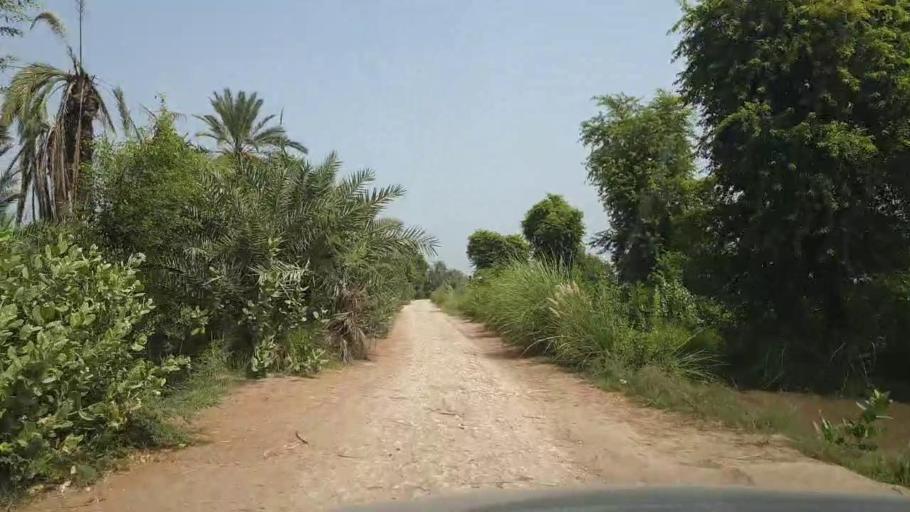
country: PK
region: Sindh
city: Madeji
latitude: 27.7924
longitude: 68.5301
